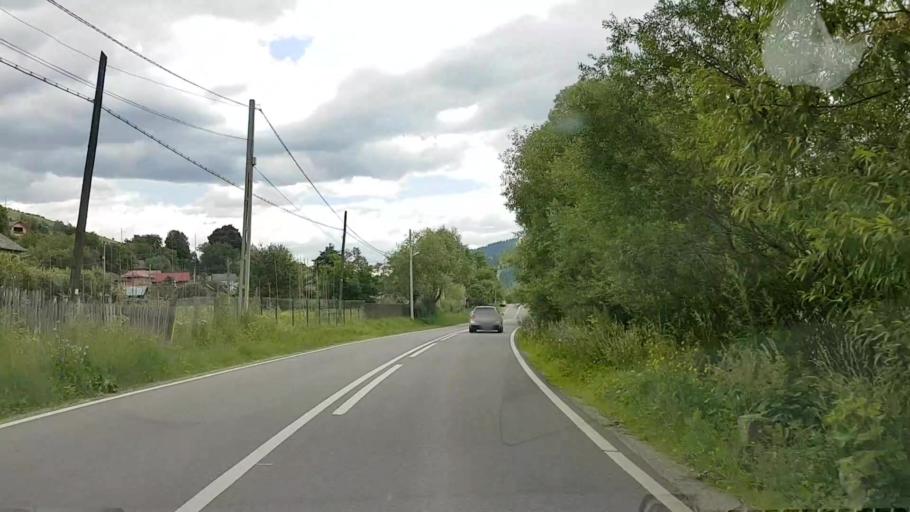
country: RO
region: Neamt
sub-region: Comuna Farcasa
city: Farcasa
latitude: 47.1689
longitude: 25.8023
